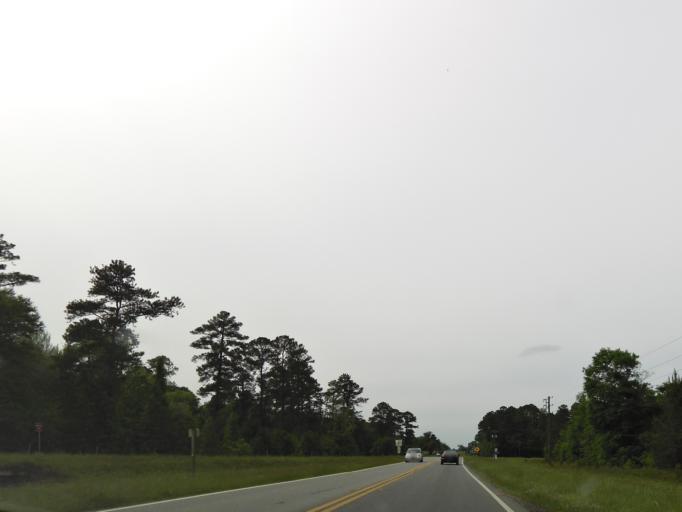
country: US
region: Georgia
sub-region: Bleckley County
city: Cochran
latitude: 32.4189
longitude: -83.3556
